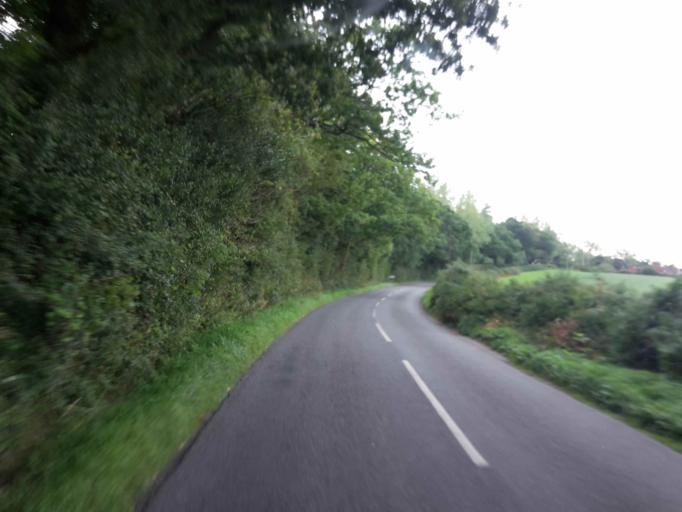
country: GB
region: England
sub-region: West Sussex
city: Rudgwick
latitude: 51.0692
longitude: -0.4480
